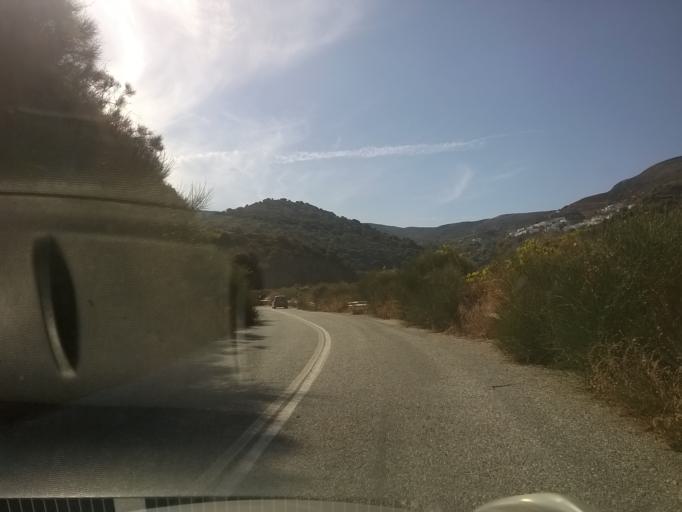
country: GR
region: South Aegean
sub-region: Nomos Kykladon
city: Filotion
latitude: 37.1447
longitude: 25.5434
